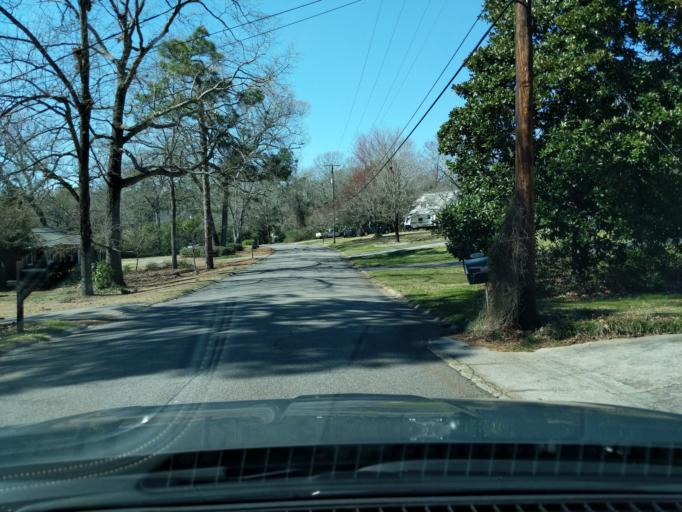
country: US
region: South Carolina
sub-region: Aiken County
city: Aiken
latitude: 33.5292
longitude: -81.7319
